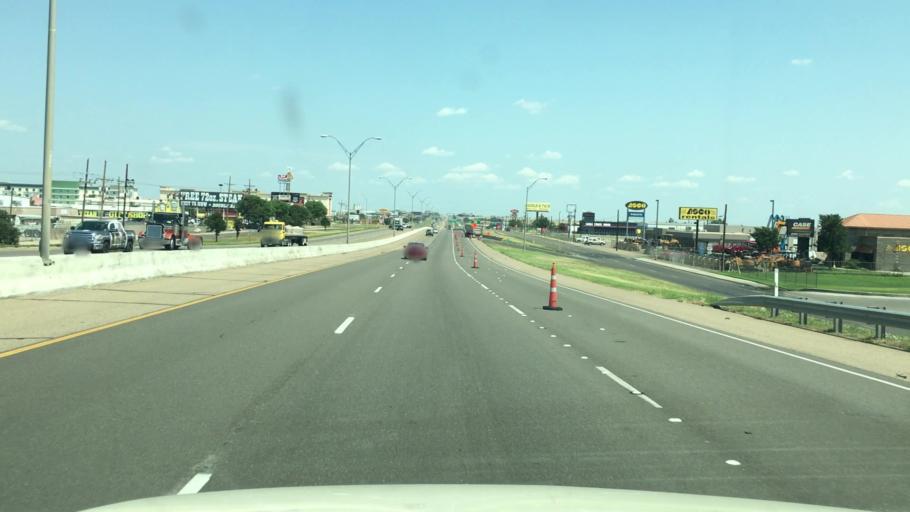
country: US
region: Texas
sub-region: Potter County
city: Amarillo
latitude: 35.1926
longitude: -101.7584
